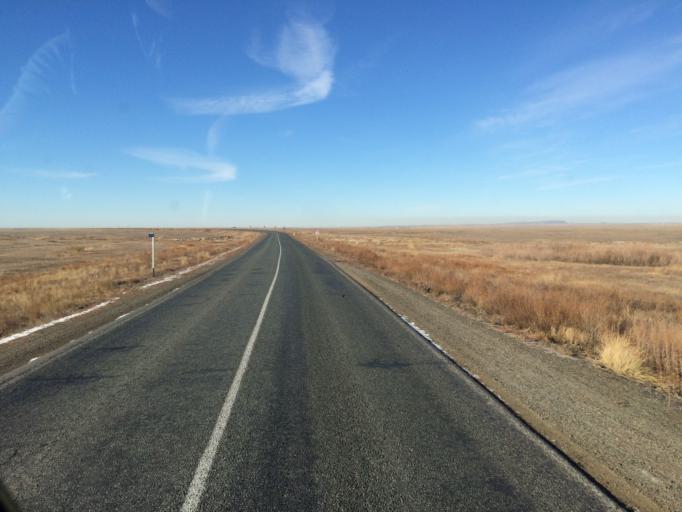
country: KZ
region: Aqtoebe
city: Khromtau
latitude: 50.1857
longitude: 58.6730
